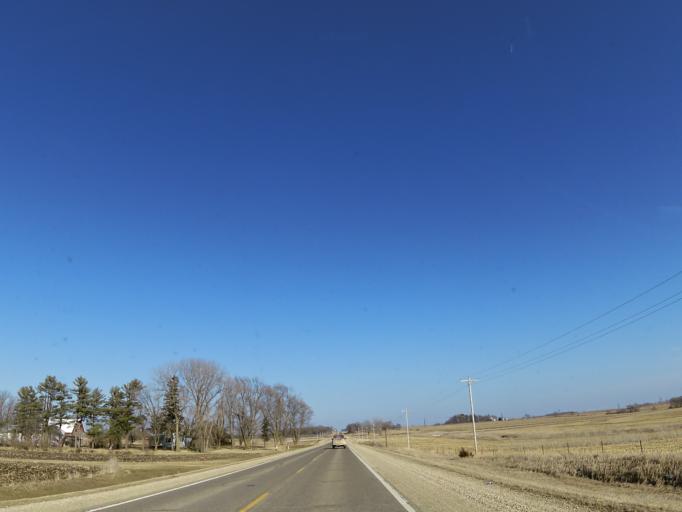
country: US
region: Iowa
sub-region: Worth County
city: Northwood
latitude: 43.4443
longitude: -93.3116
